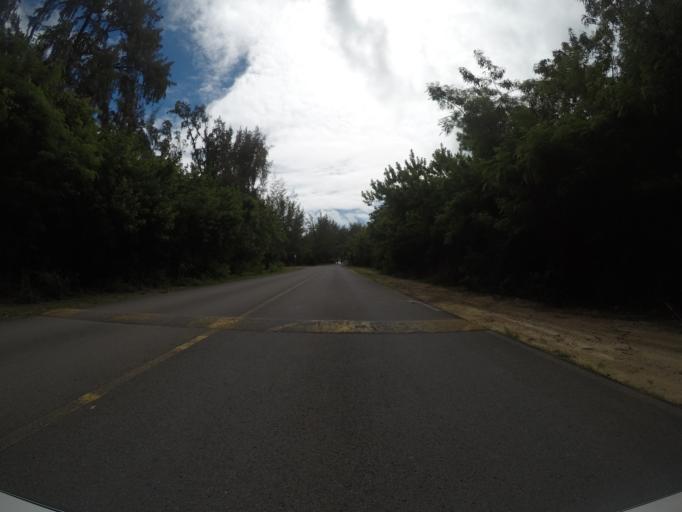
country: US
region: Hawaii
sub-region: Honolulu County
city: Waimanalo Beach
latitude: 21.3441
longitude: -157.7055
